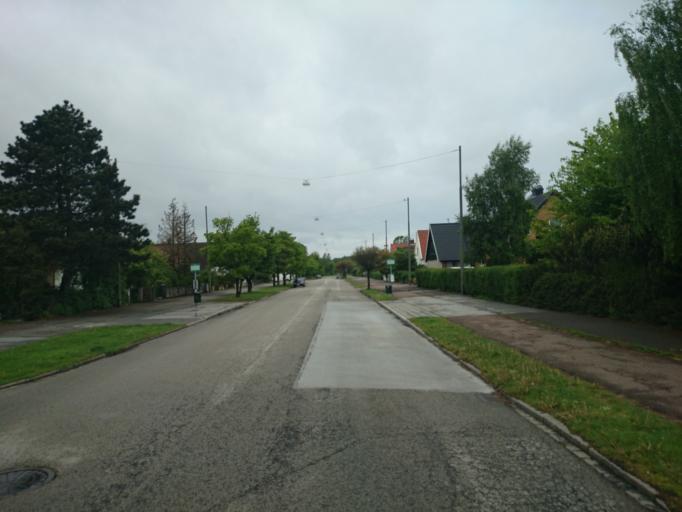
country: SE
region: Skane
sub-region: Burlovs Kommun
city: Arloev
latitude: 55.6104
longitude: 13.0744
